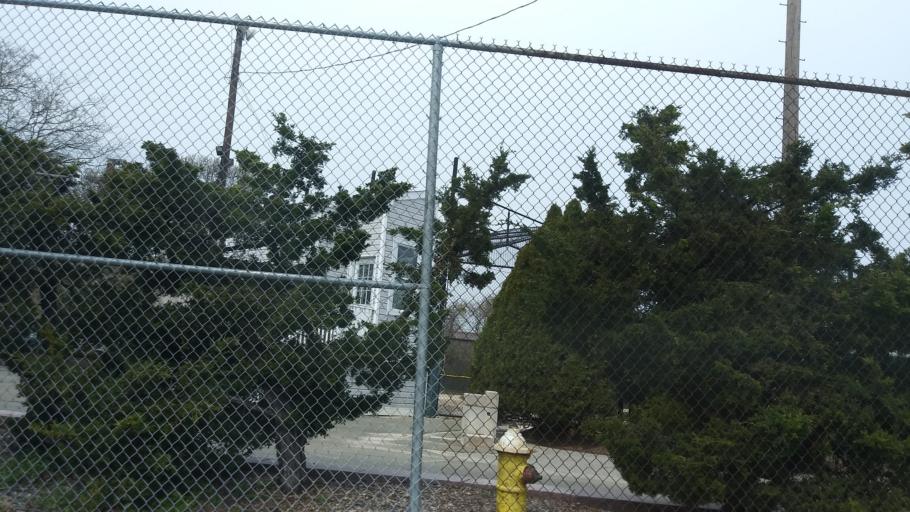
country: US
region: New York
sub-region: Nassau County
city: Rockville Centre
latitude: 40.6572
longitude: -73.6404
